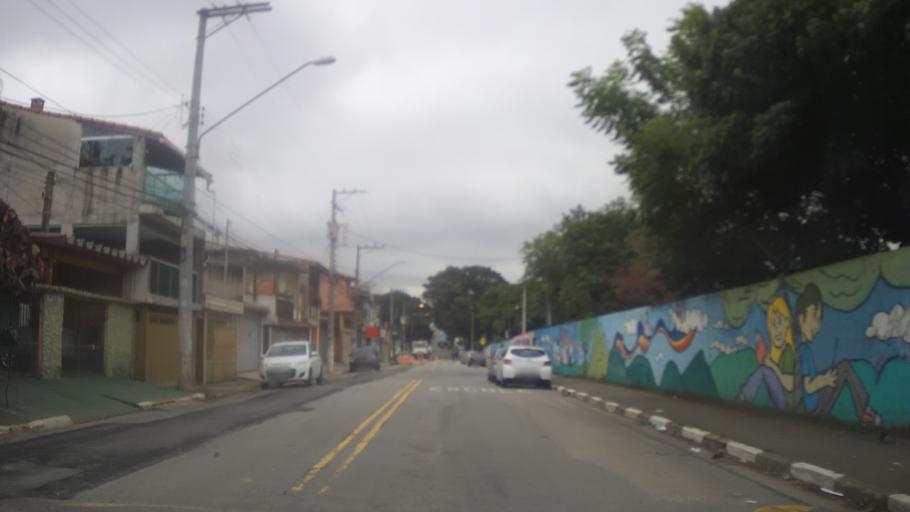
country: BR
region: Sao Paulo
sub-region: Guarulhos
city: Guarulhos
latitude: -23.4511
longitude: -46.5257
